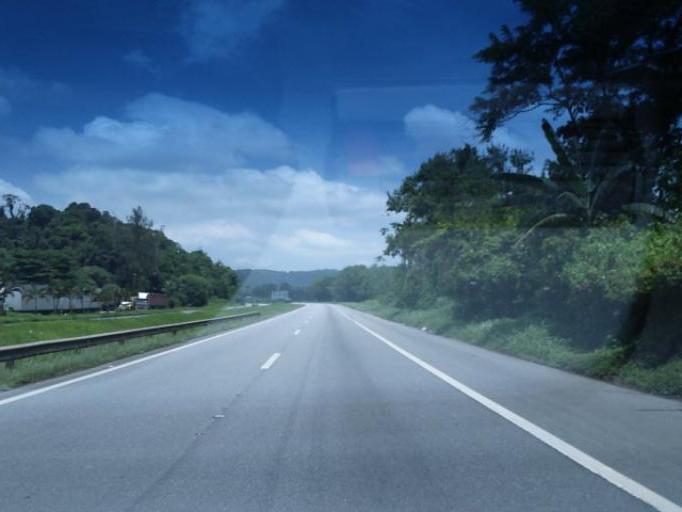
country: BR
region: Sao Paulo
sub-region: Miracatu
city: Miracatu
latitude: -24.1973
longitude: -47.3665
